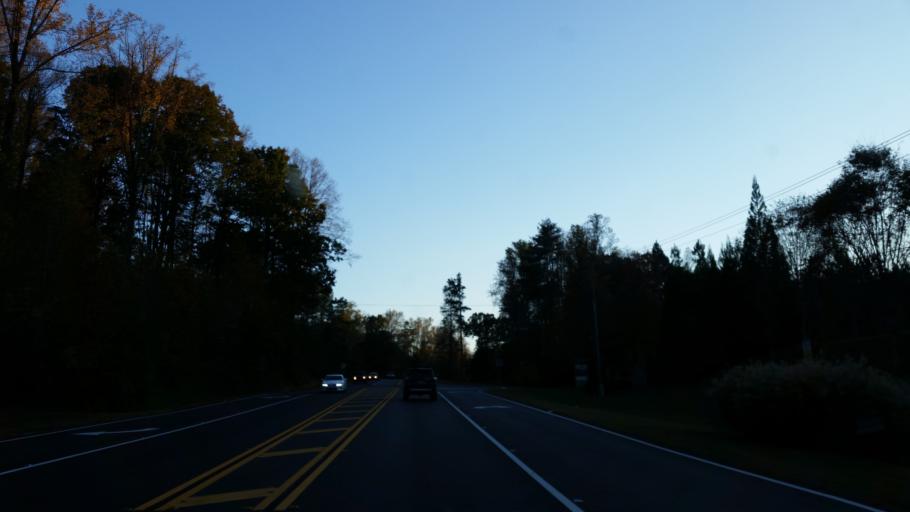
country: US
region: Georgia
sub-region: Lumpkin County
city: Dahlonega
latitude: 34.4911
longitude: -83.9719
